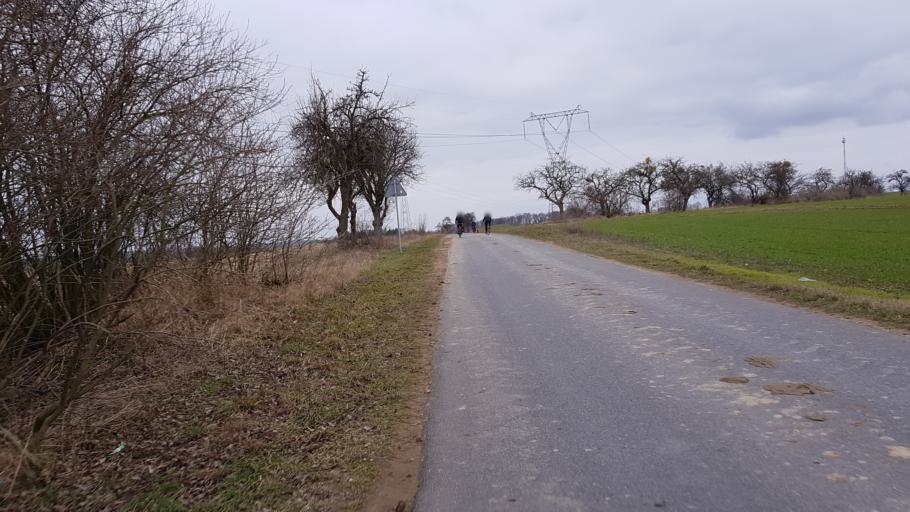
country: PL
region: West Pomeranian Voivodeship
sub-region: Powiat gryfinski
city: Banie
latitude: 53.0979
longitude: 14.6836
